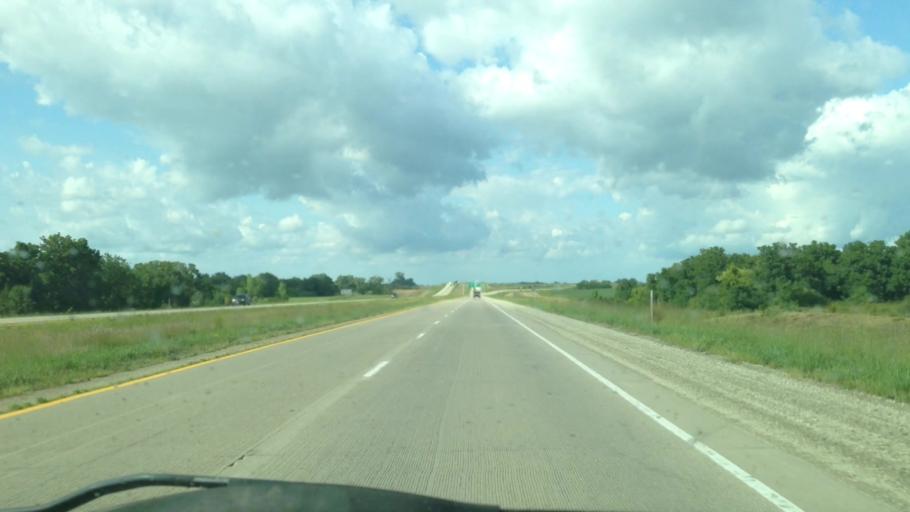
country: US
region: Illinois
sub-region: Hancock County
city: Nauvoo
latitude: 40.5982
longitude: -91.5621
